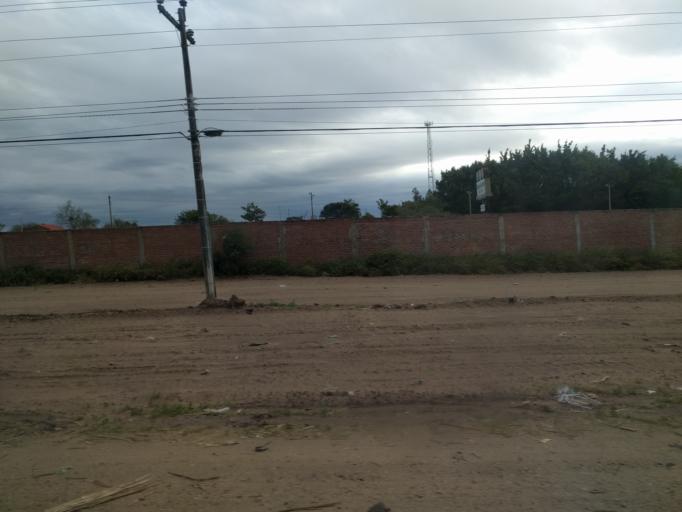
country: BO
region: Santa Cruz
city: La Belgica
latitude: -17.6339
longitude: -63.1581
